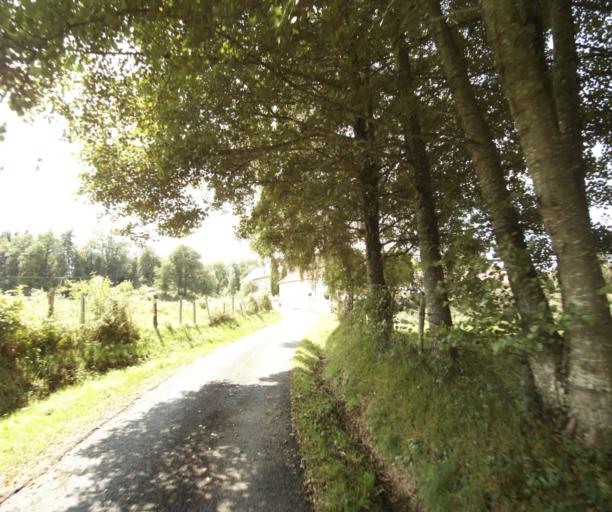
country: FR
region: Limousin
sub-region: Departement de la Correze
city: Sainte-Fortunade
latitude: 45.2079
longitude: 1.8153
